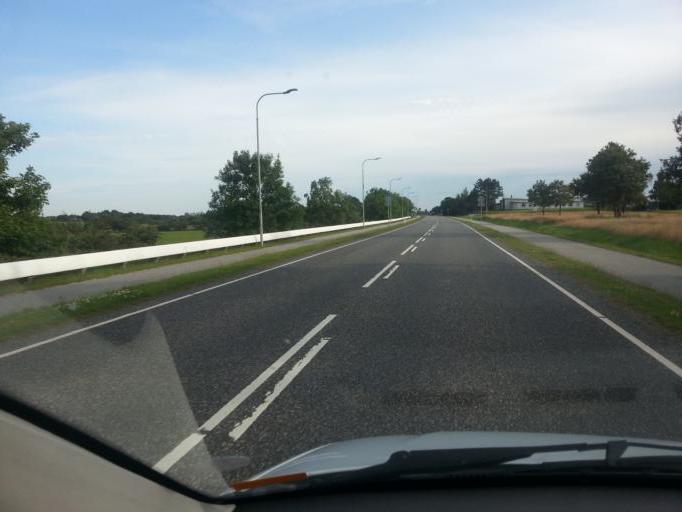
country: DK
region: South Denmark
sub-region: Vejen Kommune
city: Holsted
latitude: 55.4977
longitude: 8.9157
